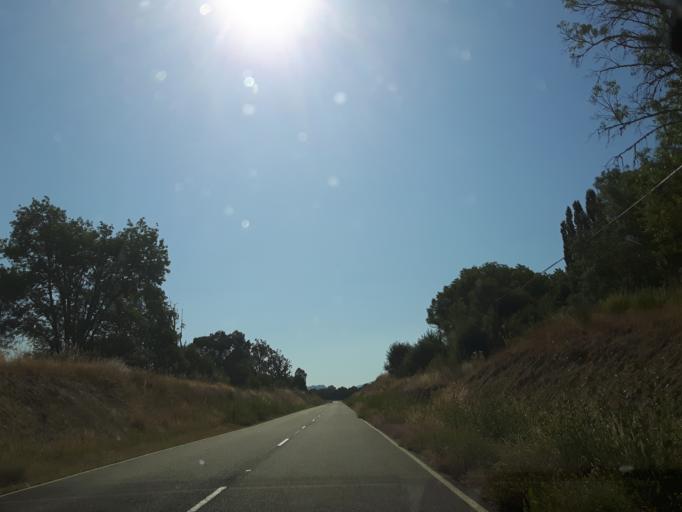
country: ES
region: Castille and Leon
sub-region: Provincia de Salamanca
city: Valdehijaderos
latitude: 40.4209
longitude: -5.8624
